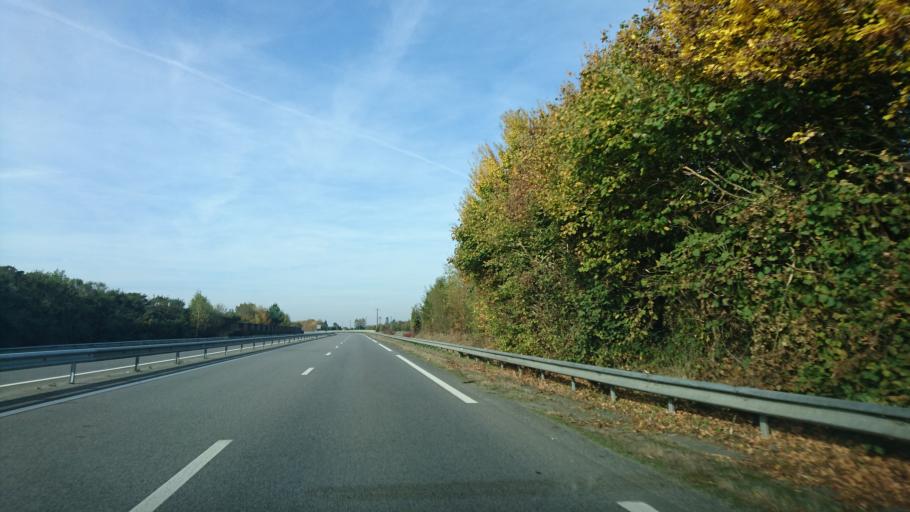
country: FR
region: Brittany
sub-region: Departement d'Ille-et-Vilaine
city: Corps-Nuds
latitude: 47.9831
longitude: -1.5682
